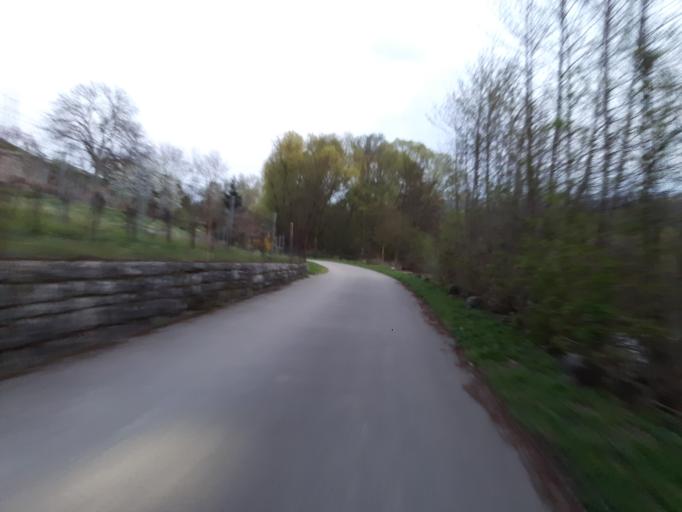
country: DE
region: Baden-Wuerttemberg
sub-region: Regierungsbezirk Stuttgart
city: Kirchheim am Neckar
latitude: 49.0474
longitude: 9.1593
